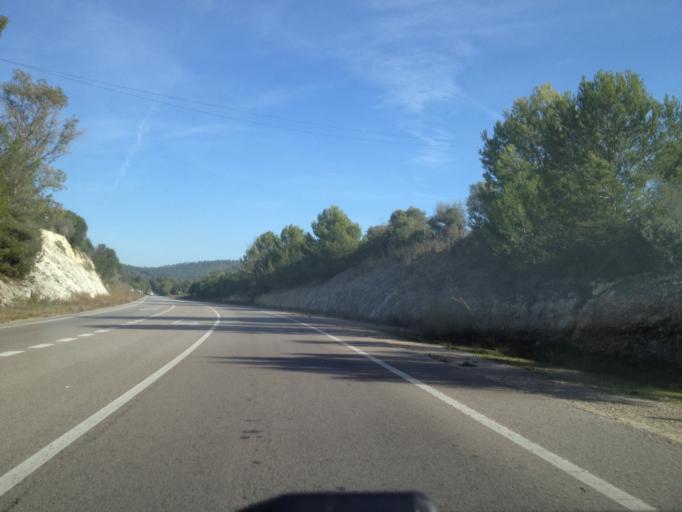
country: ES
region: Balearic Islands
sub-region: Illes Balears
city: Son Servera
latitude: 39.6446
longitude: 3.3767
